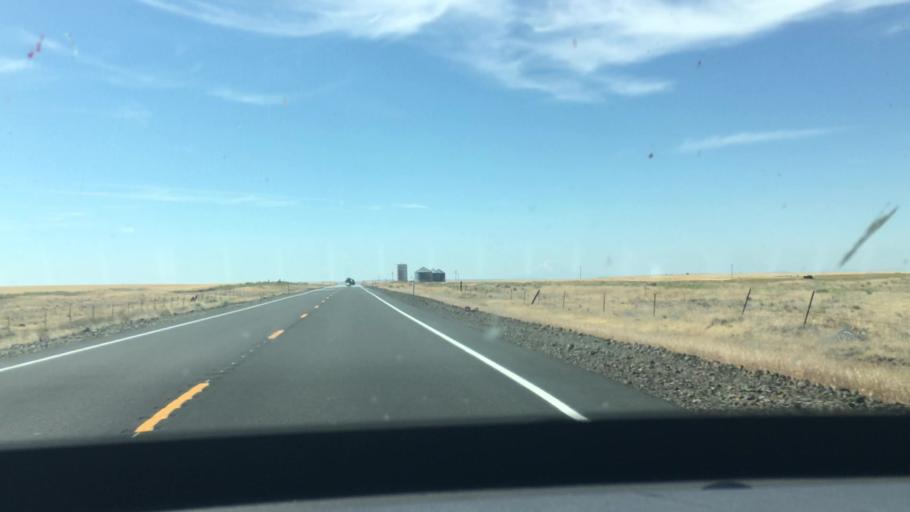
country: US
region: Oregon
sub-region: Sherman County
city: Moro
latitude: 45.2963
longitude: -120.7564
